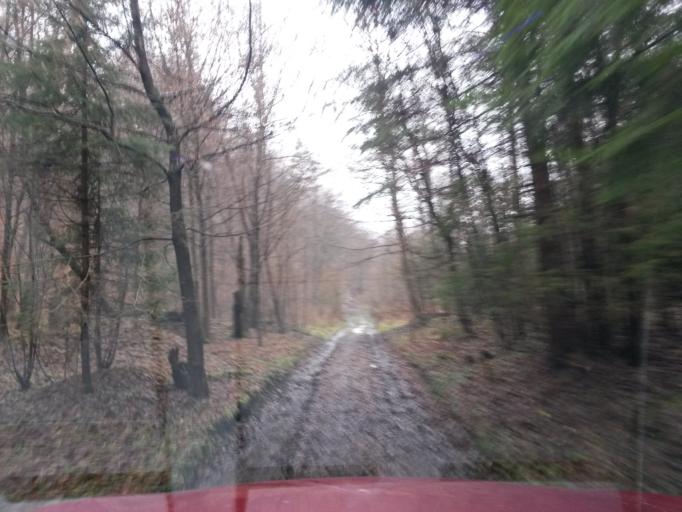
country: SK
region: Kosicky
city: Dobsina
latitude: 48.7450
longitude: 20.4082
